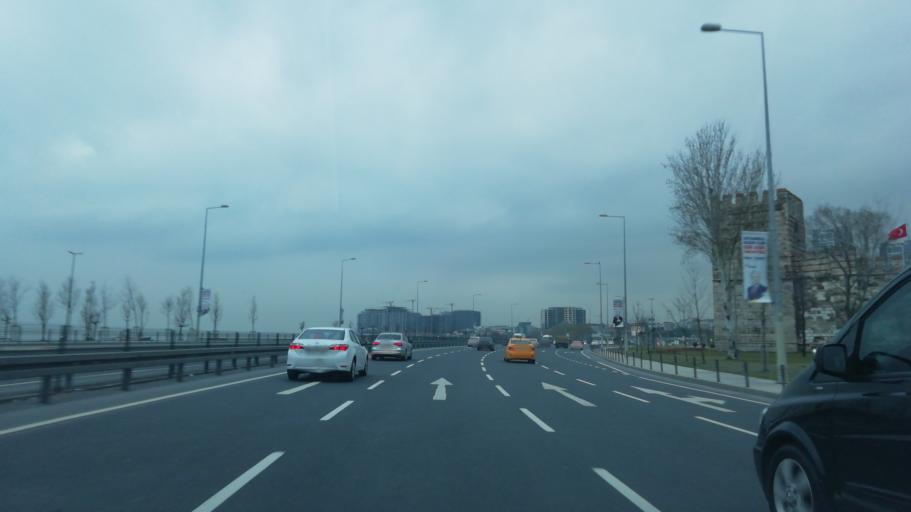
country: TR
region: Istanbul
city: Zeytinburnu
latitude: 40.9884
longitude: 28.9223
